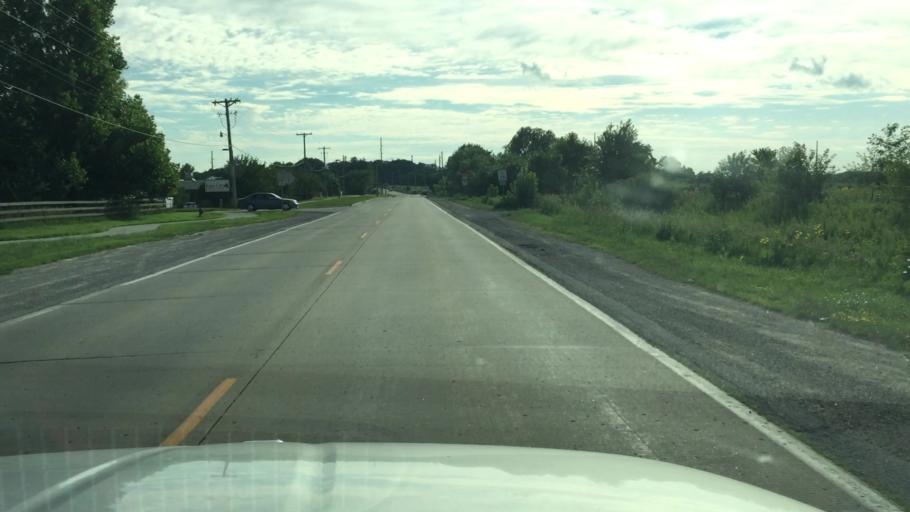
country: US
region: Iowa
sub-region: Johnson County
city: Iowa City
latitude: 41.6697
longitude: -91.4790
